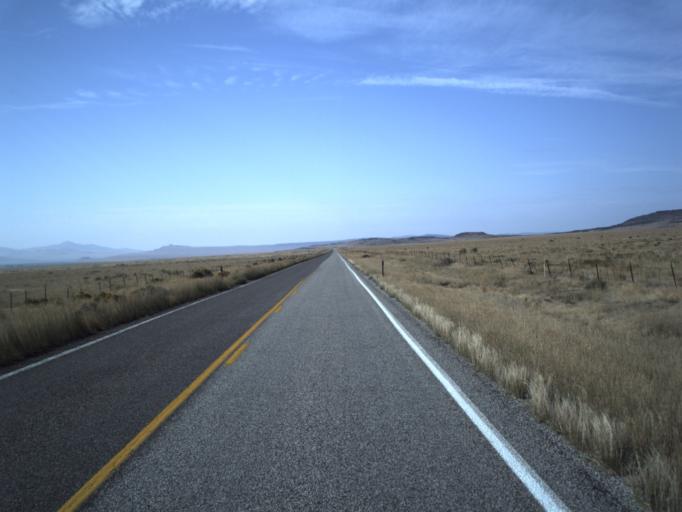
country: US
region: Idaho
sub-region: Oneida County
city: Malad City
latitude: 41.8823
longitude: -113.1167
